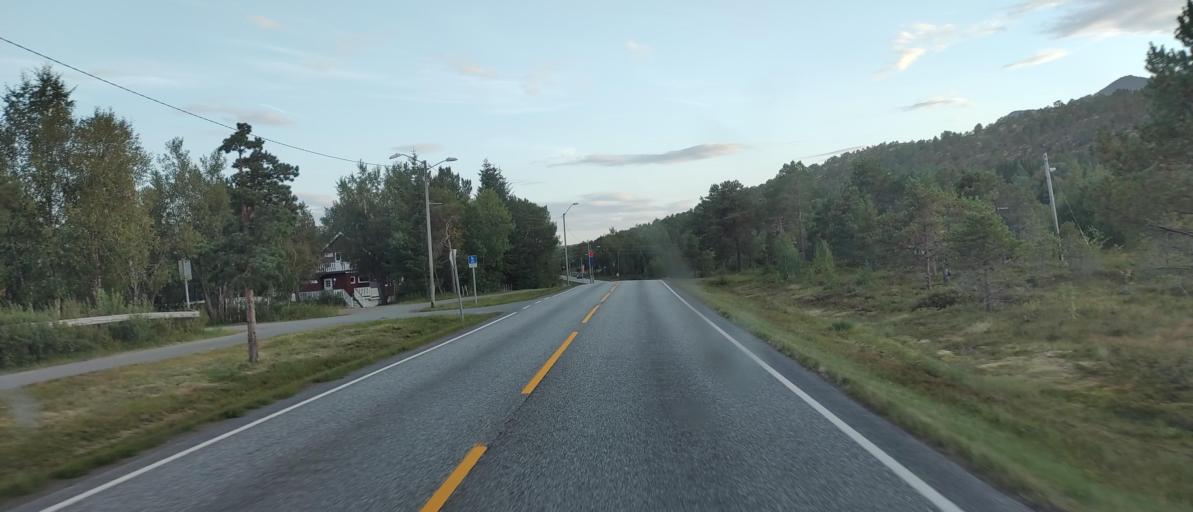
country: NO
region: Nordland
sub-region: Lodingen
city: Lodingen
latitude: 68.2006
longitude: 16.0605
